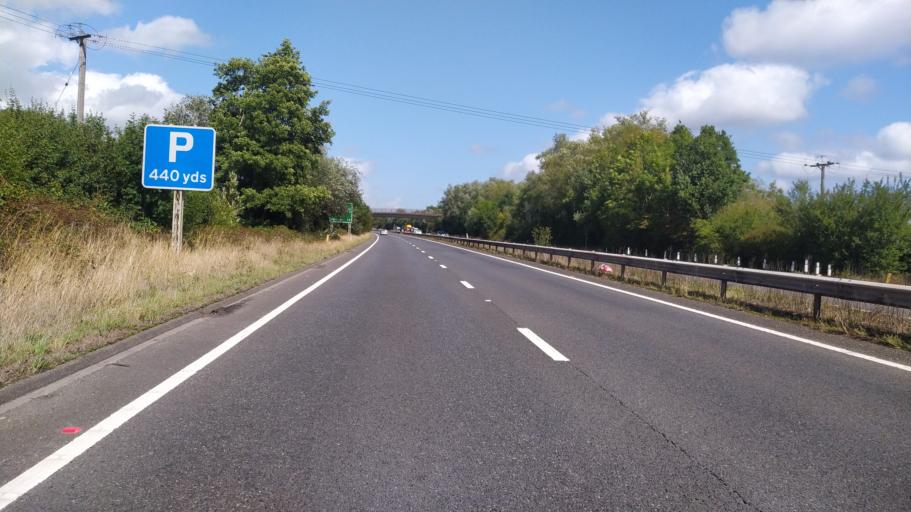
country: GB
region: England
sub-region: Hampshire
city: Liss
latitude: 51.0397
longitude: -0.9038
